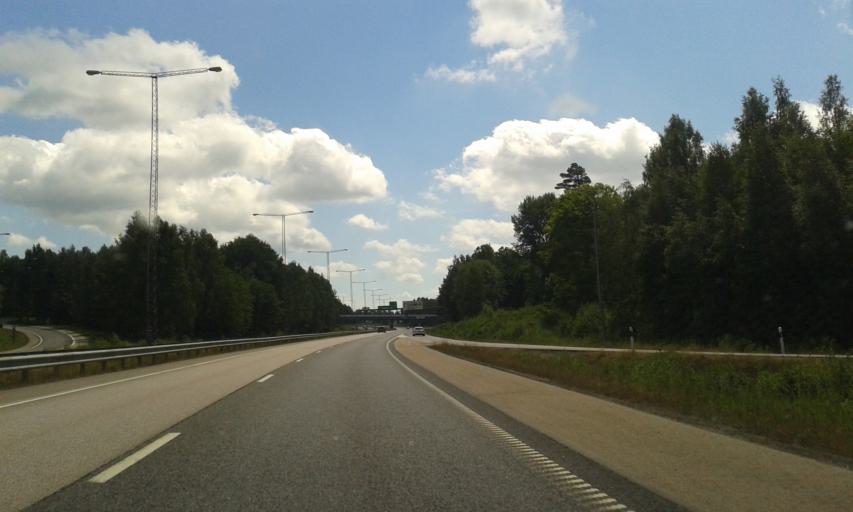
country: SE
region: Kronoberg
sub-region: Vaxjo Kommun
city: Vaexjoe
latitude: 56.8880
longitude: 14.7557
